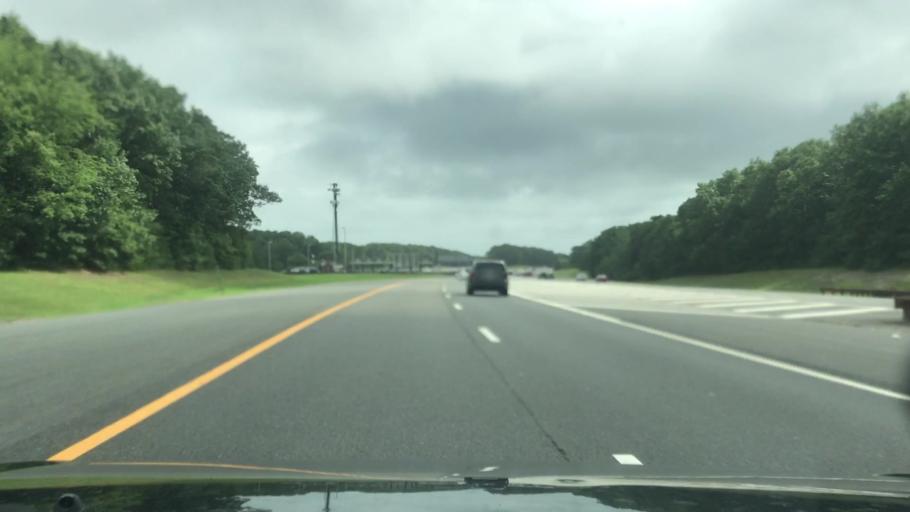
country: US
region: New Jersey
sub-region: Monmouth County
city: Eatontown
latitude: 40.2543
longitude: -74.0816
